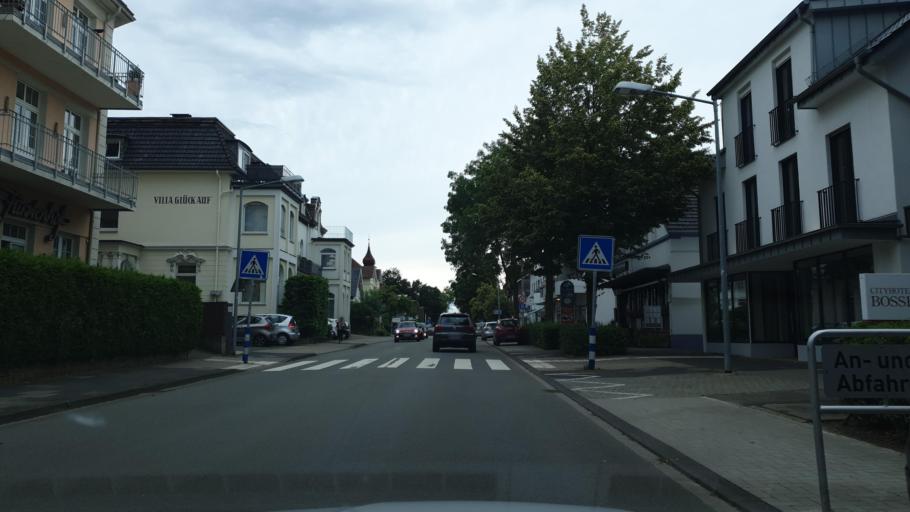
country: DE
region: North Rhine-Westphalia
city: Bad Oeynhausen
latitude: 52.2022
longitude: 8.7901
